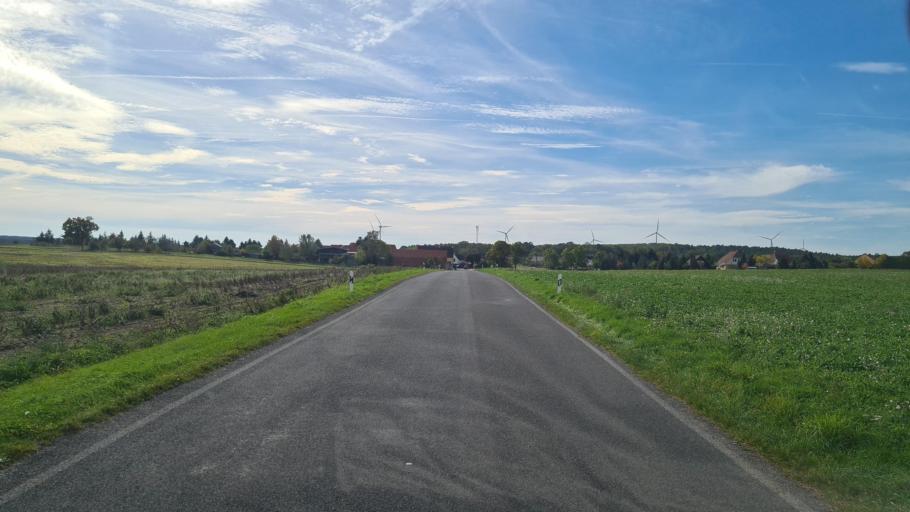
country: DE
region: Brandenburg
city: Linthe
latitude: 52.0939
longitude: 12.7584
